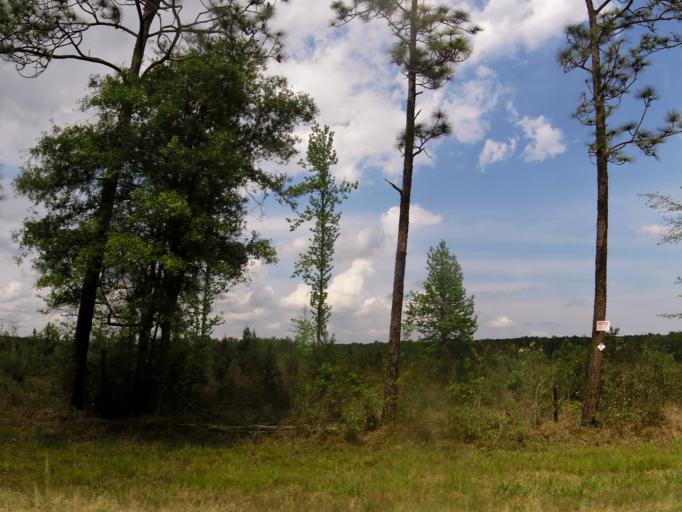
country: US
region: Florida
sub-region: Nassau County
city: Hilliard
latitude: 30.8165
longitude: -81.8470
